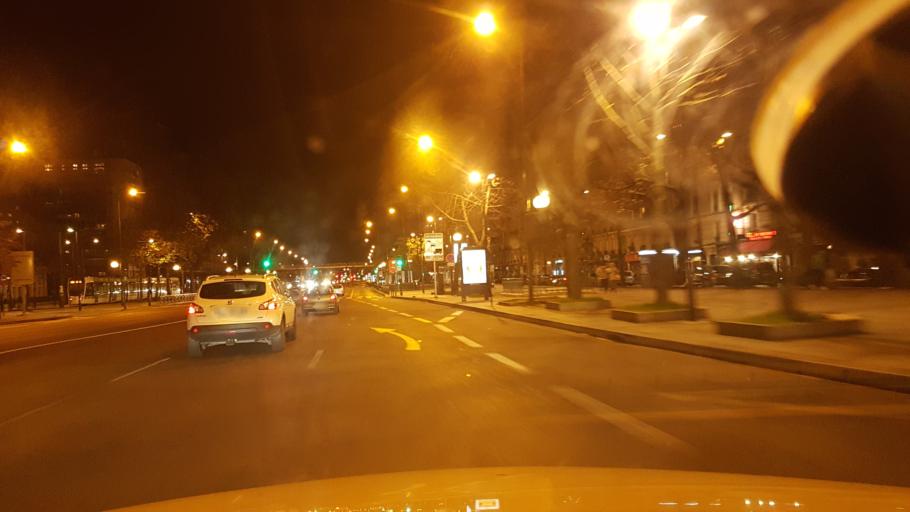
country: FR
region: Ile-de-France
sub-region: Departement du Val-de-Marne
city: Saint-Mande
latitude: 48.8474
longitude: 2.4069
